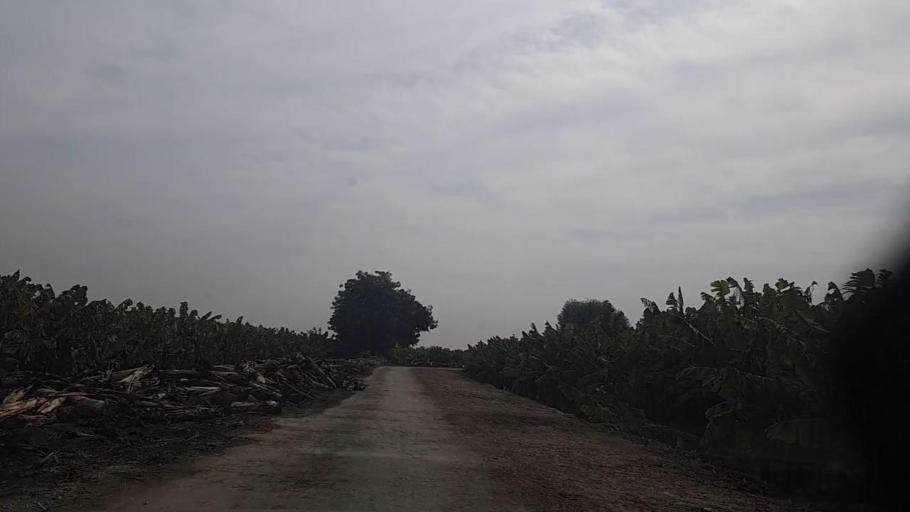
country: PK
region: Sindh
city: Sakrand
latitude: 26.2405
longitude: 68.2967
